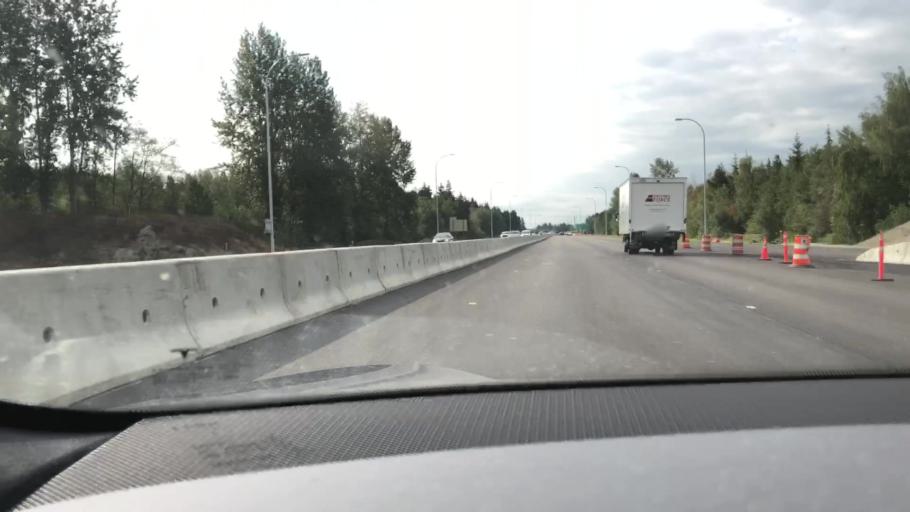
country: CA
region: British Columbia
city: Delta
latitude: 49.1321
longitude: -122.9285
